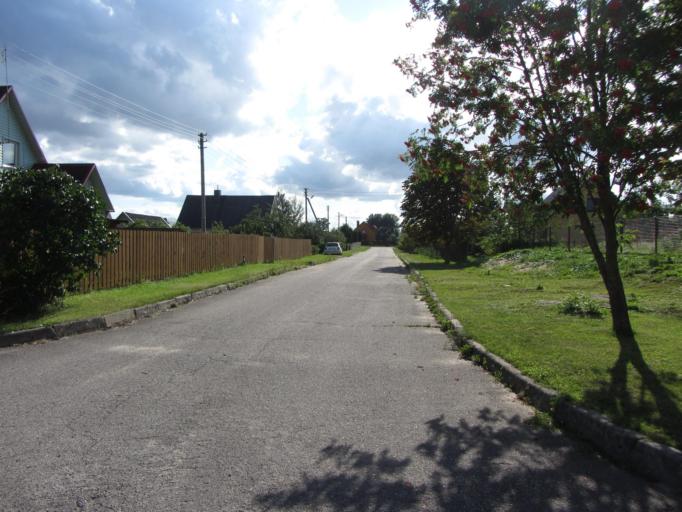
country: LT
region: Vilnius County
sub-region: Vilniaus Rajonas
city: Vievis
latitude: 54.7616
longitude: 24.8002
